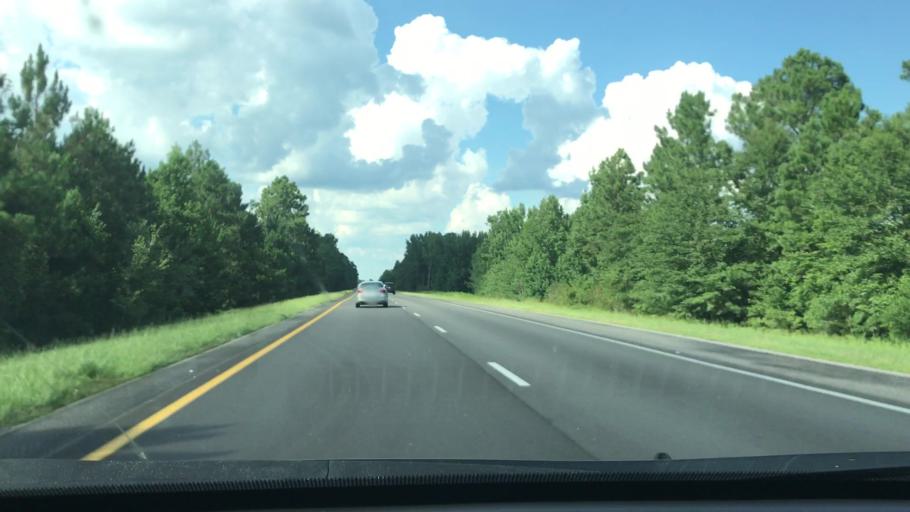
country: US
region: South Carolina
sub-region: Clarendon County
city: Manning
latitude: 33.8468
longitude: -80.1208
